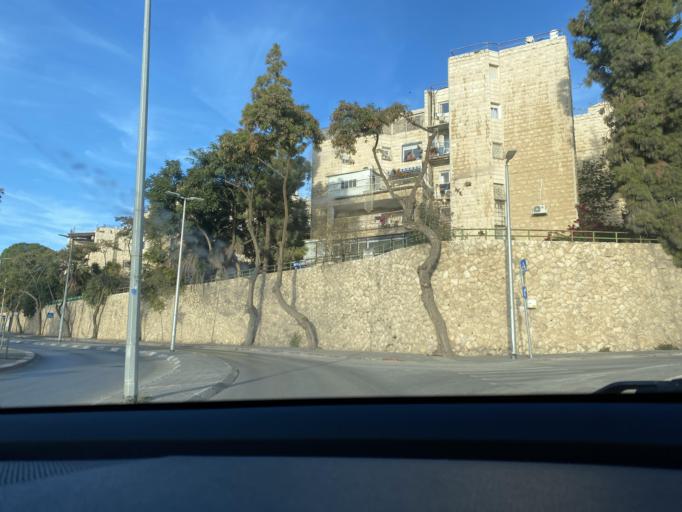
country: PS
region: West Bank
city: Ash Shaykh Sa`d
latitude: 31.7461
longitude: 35.2395
